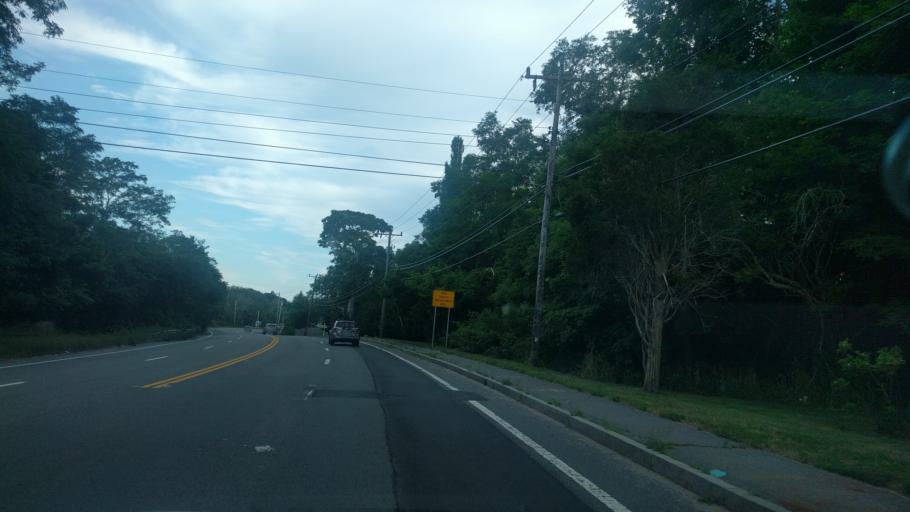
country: US
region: Massachusetts
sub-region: Barnstable County
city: Eastham
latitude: 41.8218
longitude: -69.9709
